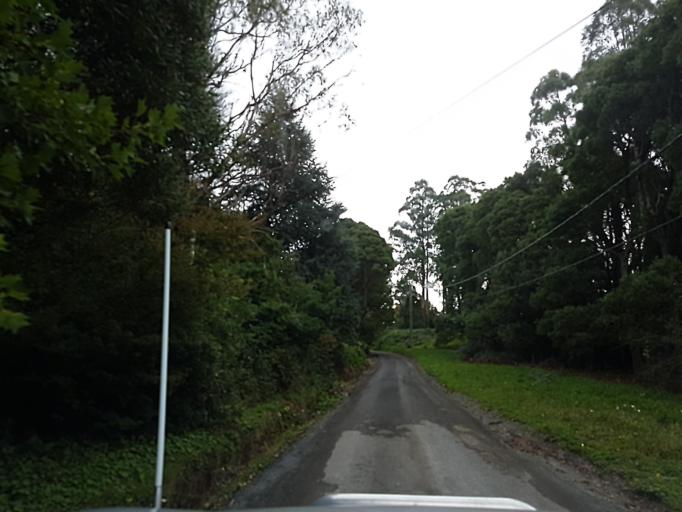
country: AU
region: Victoria
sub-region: Yarra Ranges
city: Olinda
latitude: -37.8603
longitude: 145.3804
